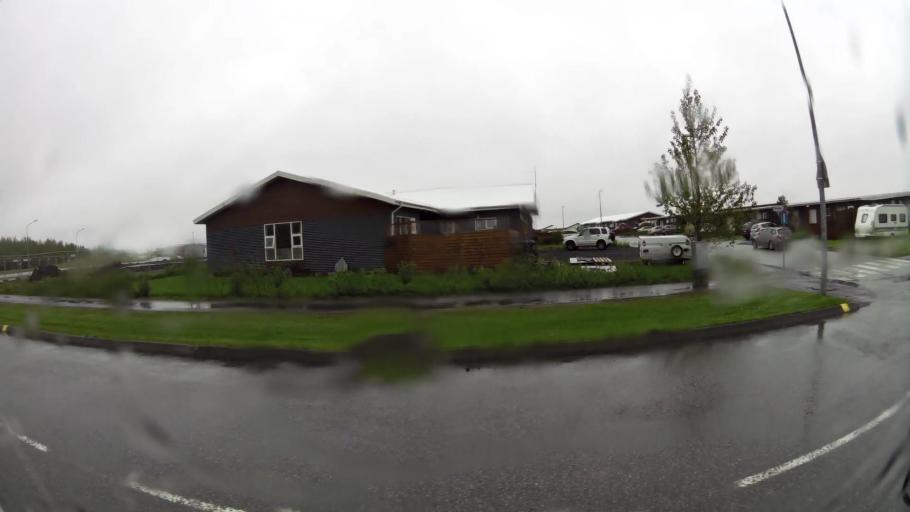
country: IS
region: South
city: Selfoss
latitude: 63.9260
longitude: -21.0071
